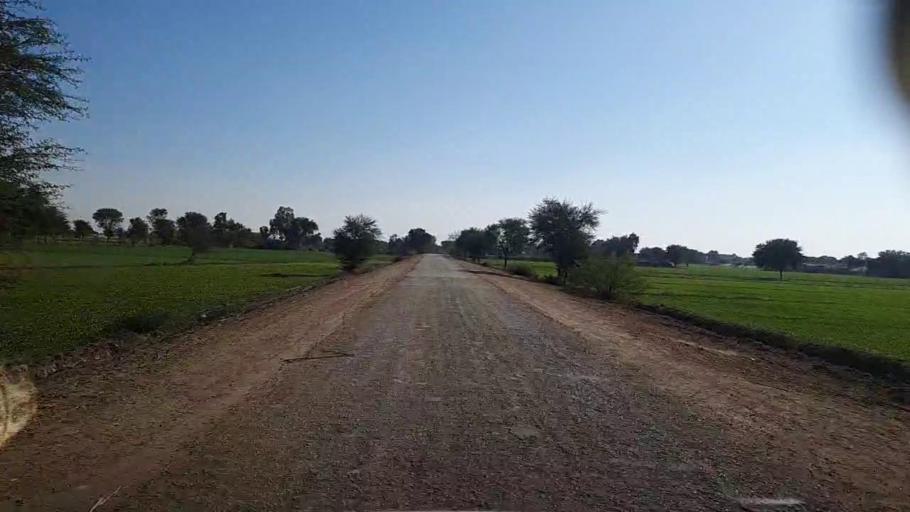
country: PK
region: Sindh
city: Khairpur
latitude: 27.9162
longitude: 69.7517
